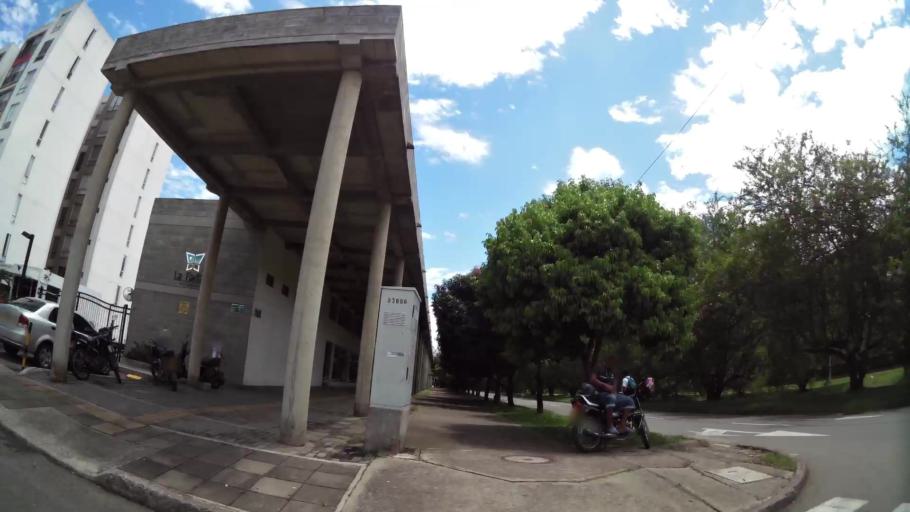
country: CO
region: Valle del Cauca
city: Cali
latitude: 3.3849
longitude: -76.5162
